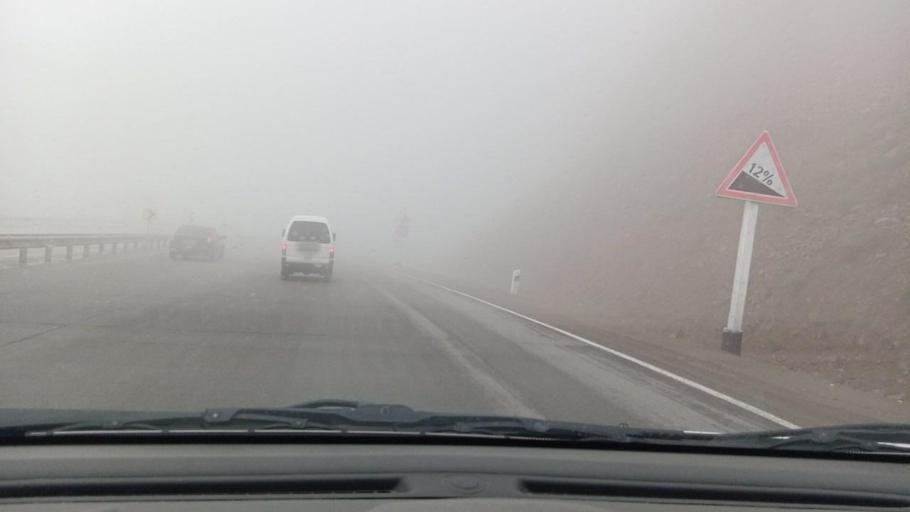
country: UZ
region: Toshkent
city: Angren
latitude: 41.1090
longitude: 70.5062
